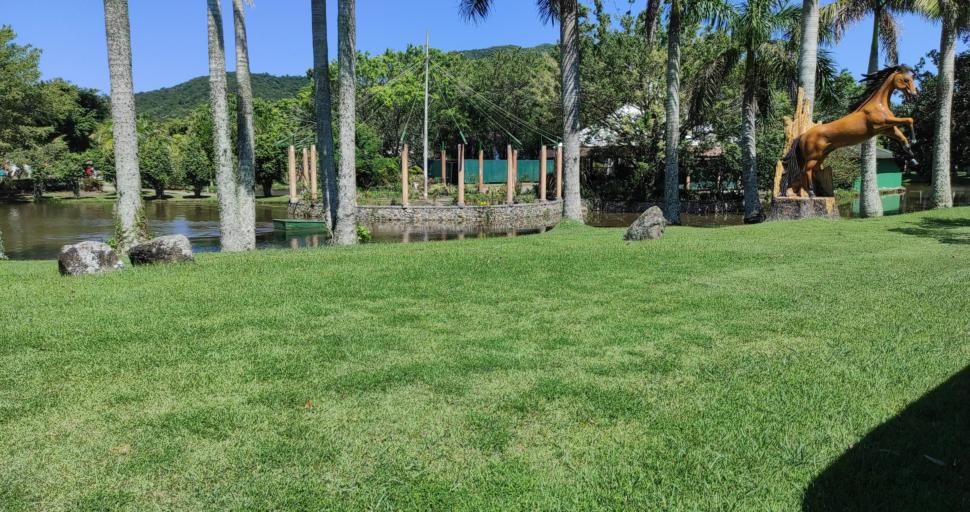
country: BR
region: Santa Catarina
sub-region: Penha
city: Penha
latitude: -26.8047
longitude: -48.6195
